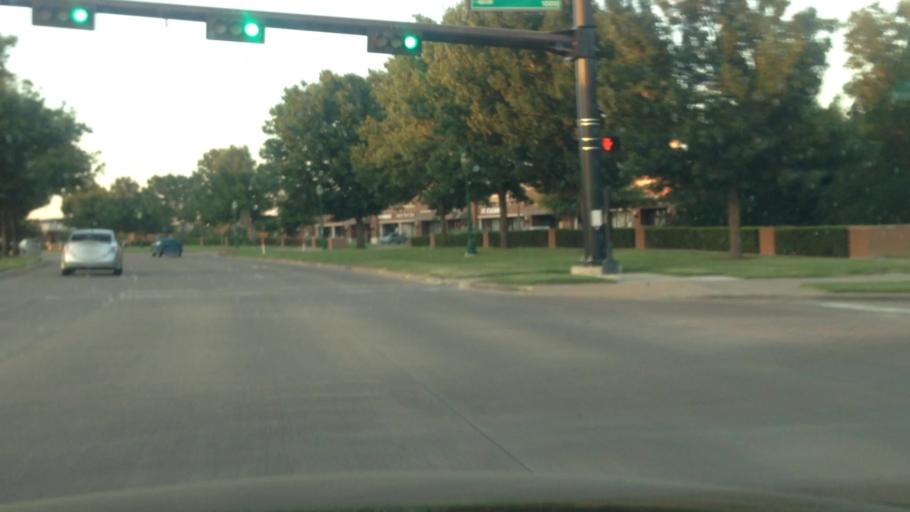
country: US
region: Texas
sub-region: Tarrant County
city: Keller
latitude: 32.9313
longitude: -97.2297
